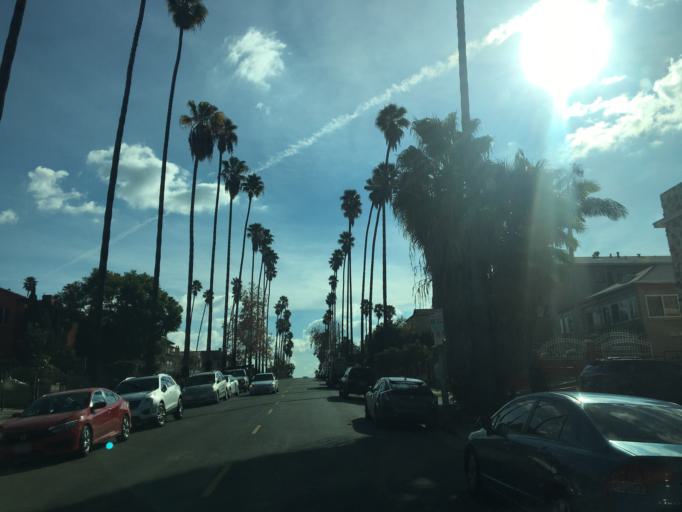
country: US
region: California
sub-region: Los Angeles County
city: Silver Lake
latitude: 34.0758
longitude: -118.2955
